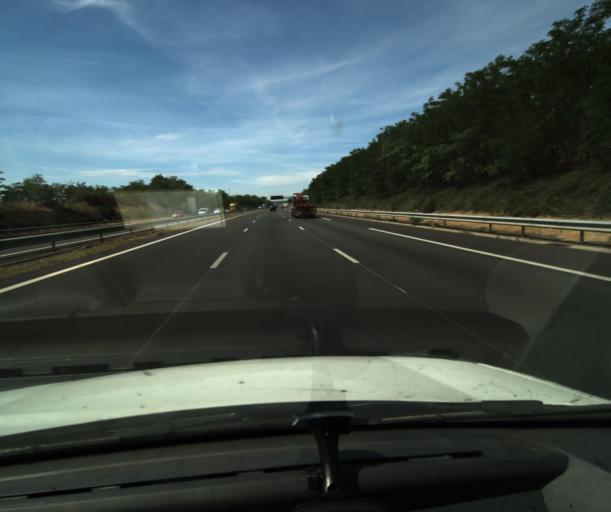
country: FR
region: Midi-Pyrenees
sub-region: Departement de la Haute-Garonne
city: Saint-Alban
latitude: 43.6952
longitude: 1.4092
